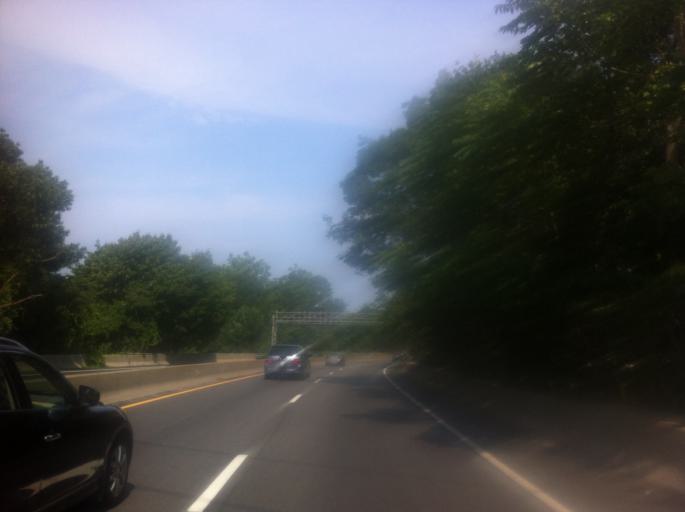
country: US
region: New York
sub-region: Nassau County
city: Jericho
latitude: 40.7906
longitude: -73.5182
